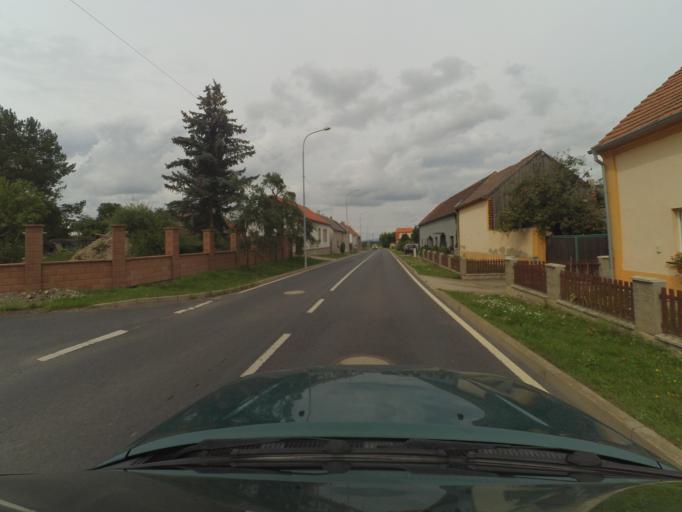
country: CZ
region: Central Bohemia
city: Revnicov
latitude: 50.2556
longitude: 13.7748
